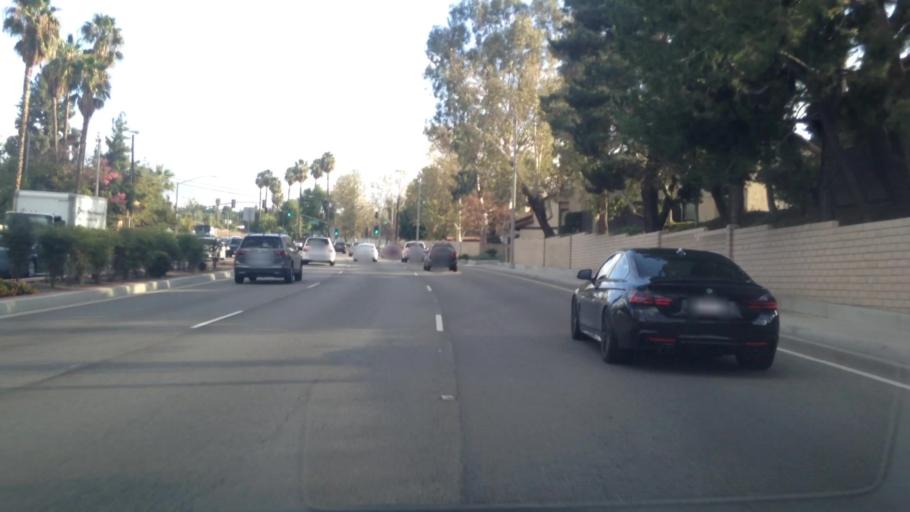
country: US
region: California
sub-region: Riverside County
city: Riverside
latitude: 33.9328
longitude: -117.3496
